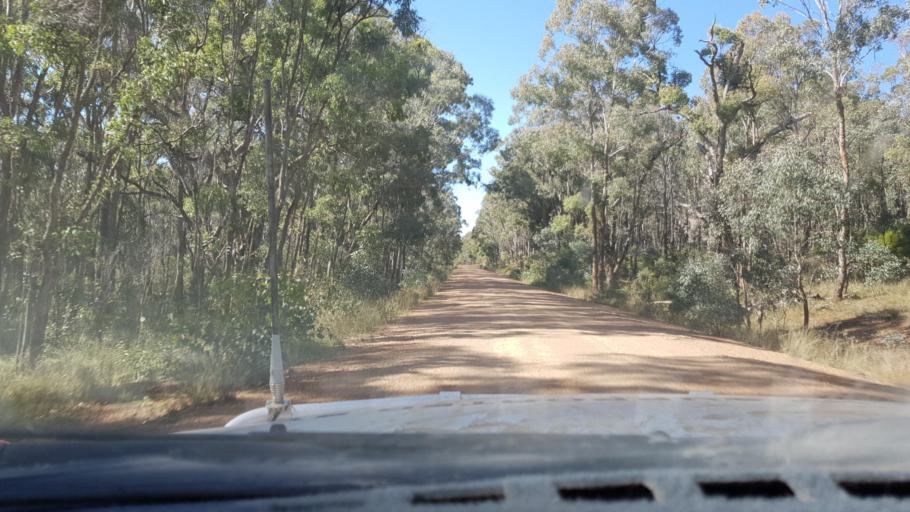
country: AU
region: New South Wales
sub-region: Tamworth Municipality
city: Manilla
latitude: -30.4576
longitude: 150.8839
